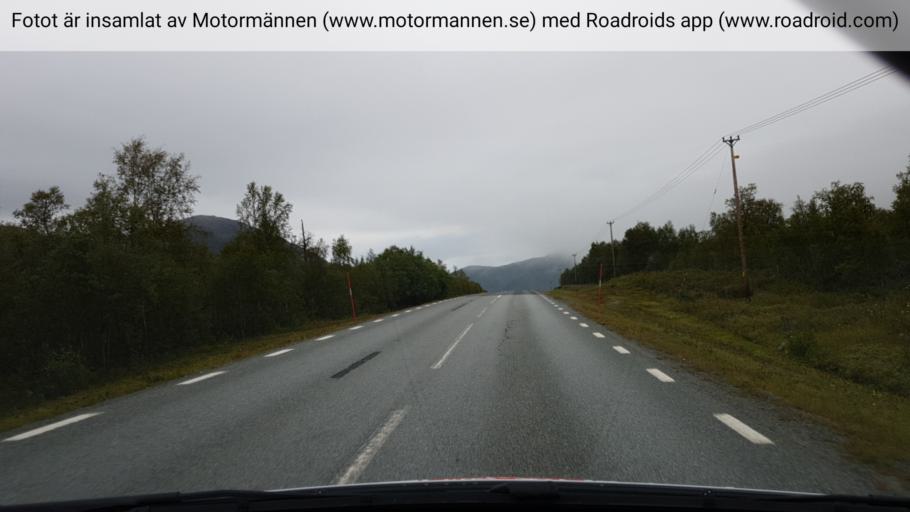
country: NO
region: Nordland
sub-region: Rana
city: Mo i Rana
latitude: 65.9153
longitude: 14.9947
